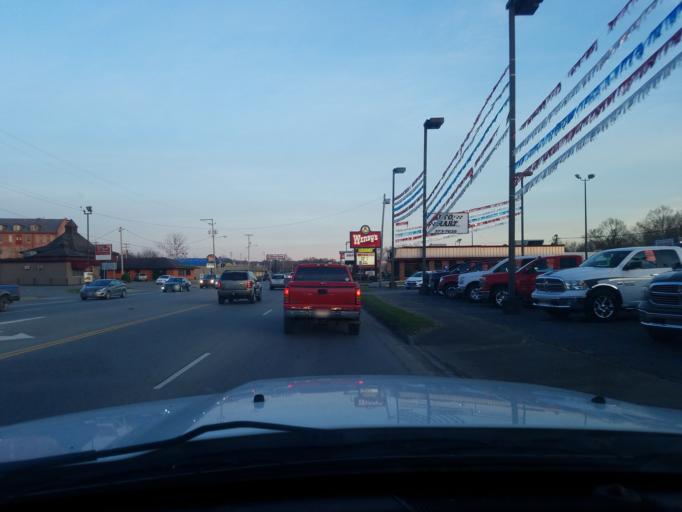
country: US
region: Ohio
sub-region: Washington County
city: Marietta
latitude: 39.4150
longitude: -81.4434
